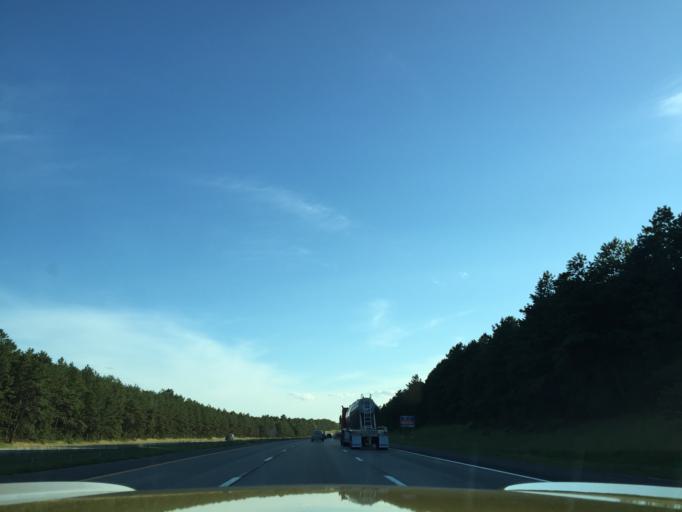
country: US
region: New York
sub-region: Suffolk County
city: Calverton
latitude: 40.8948
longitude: -72.7485
